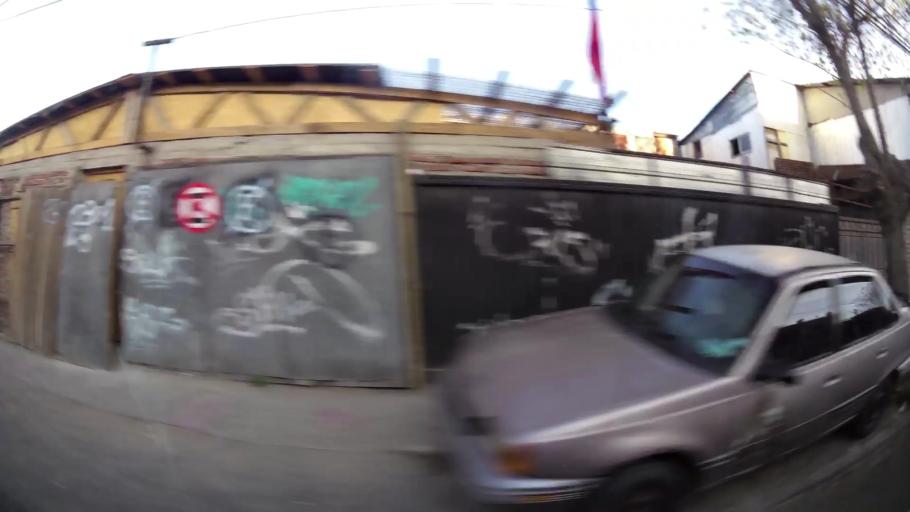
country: CL
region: Santiago Metropolitan
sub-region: Provincia de Santiago
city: Lo Prado
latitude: -33.4178
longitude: -70.7170
